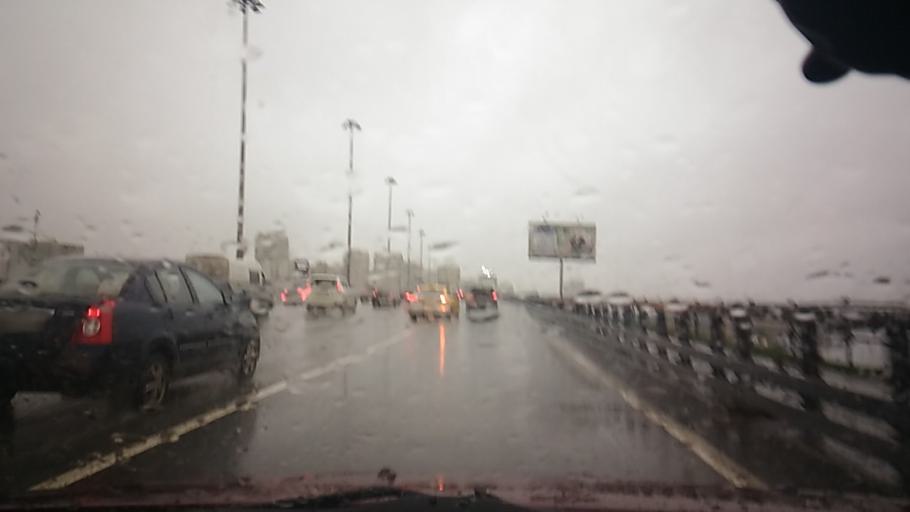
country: RU
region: Moskovskaya
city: Levoberezhnaya
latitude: 55.8747
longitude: 37.4531
